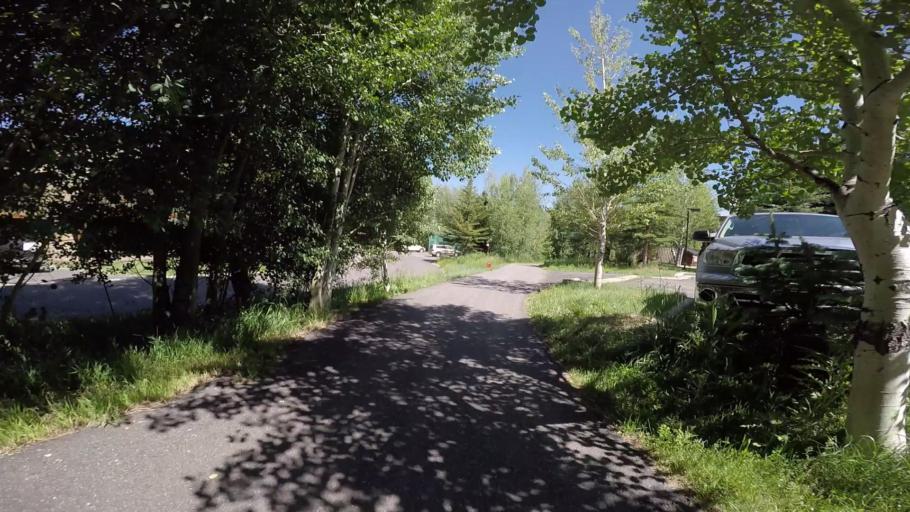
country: US
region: Utah
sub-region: Summit County
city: Park City
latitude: 40.6653
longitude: -111.5128
